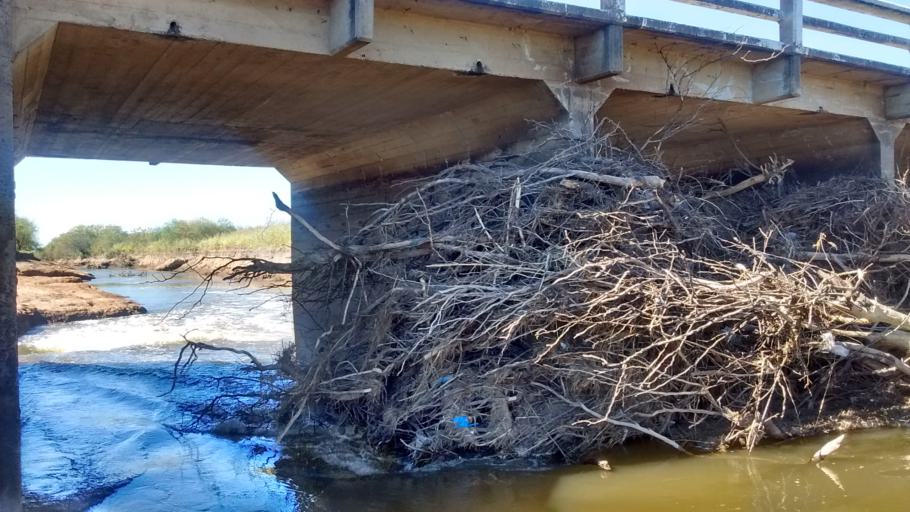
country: AR
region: Santa Fe
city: Sastre
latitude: -31.8032
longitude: -61.5698
